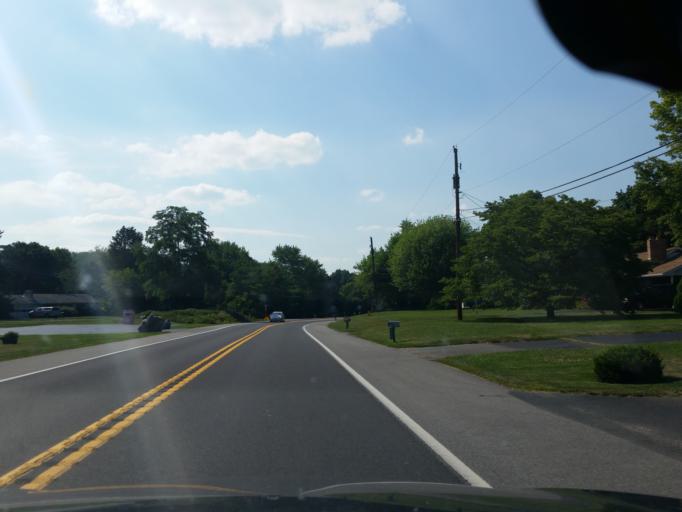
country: US
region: Pennsylvania
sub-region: Cumberland County
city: Mechanicsburg
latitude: 40.2283
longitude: -77.0300
